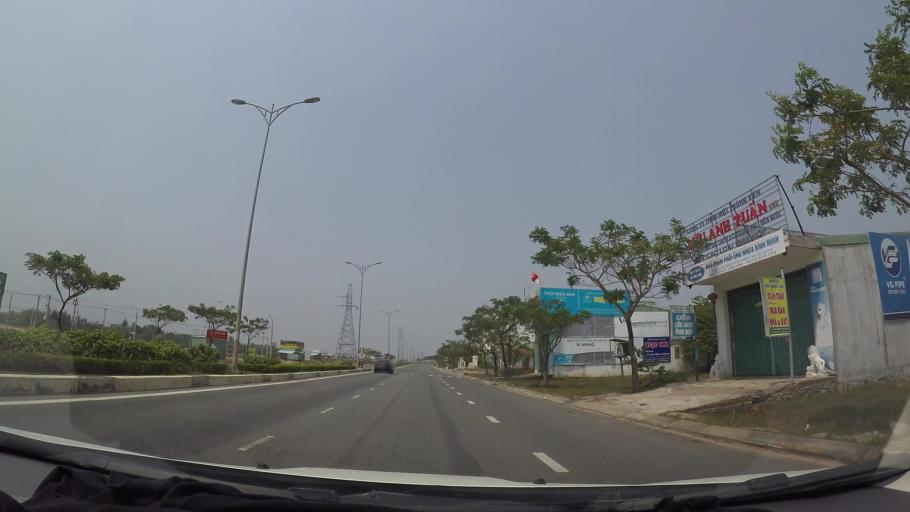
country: VN
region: Da Nang
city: Ngu Hanh Son
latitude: 15.9959
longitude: 108.2349
